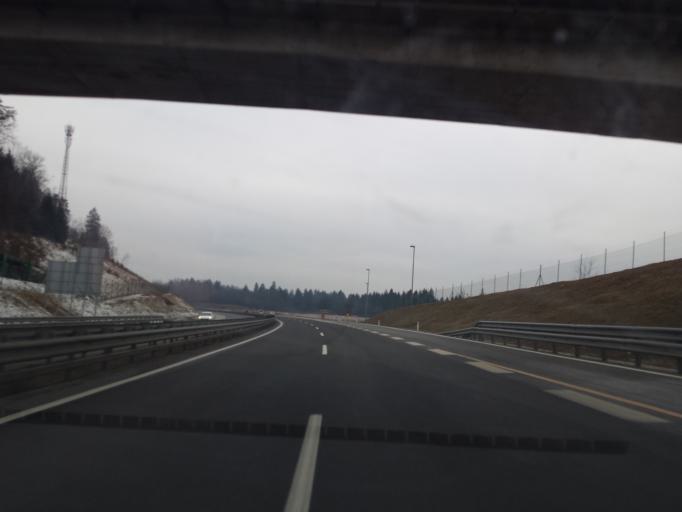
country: SI
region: Trebnje
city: Trebnje
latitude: 45.8999
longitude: 15.0516
